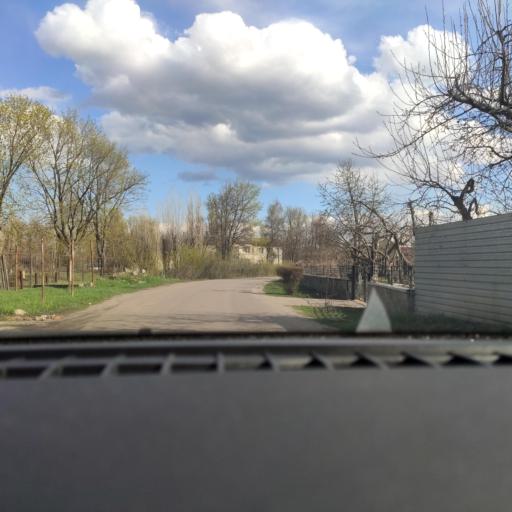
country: RU
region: Voronezj
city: Maslovka
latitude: 51.5362
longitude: 39.3317
